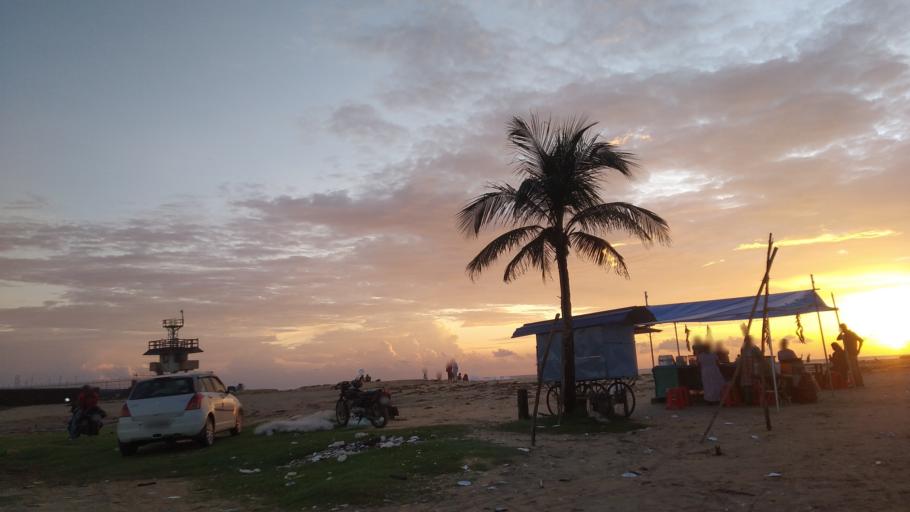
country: IN
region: Kerala
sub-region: Ernakulam
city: Cochin
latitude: 9.9985
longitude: 76.2188
